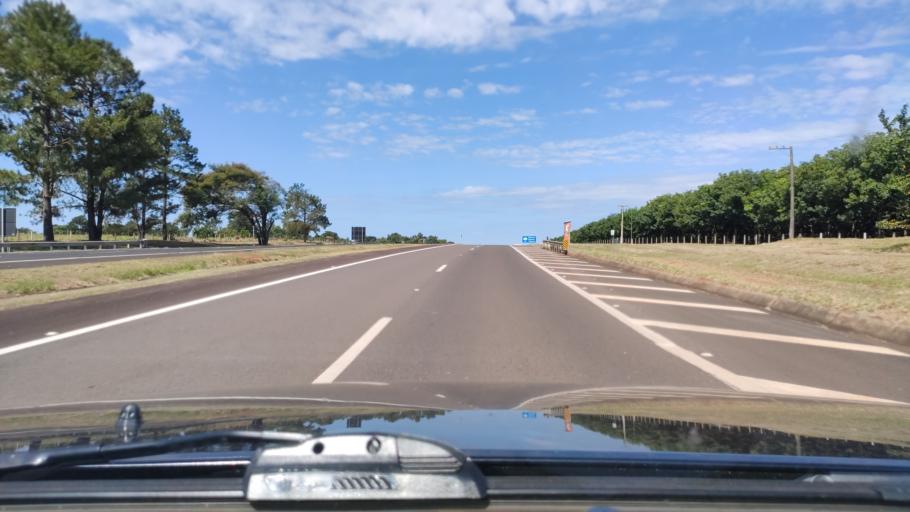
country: BR
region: Sao Paulo
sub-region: Rancharia
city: Rancharia
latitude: -22.4441
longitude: -50.9935
